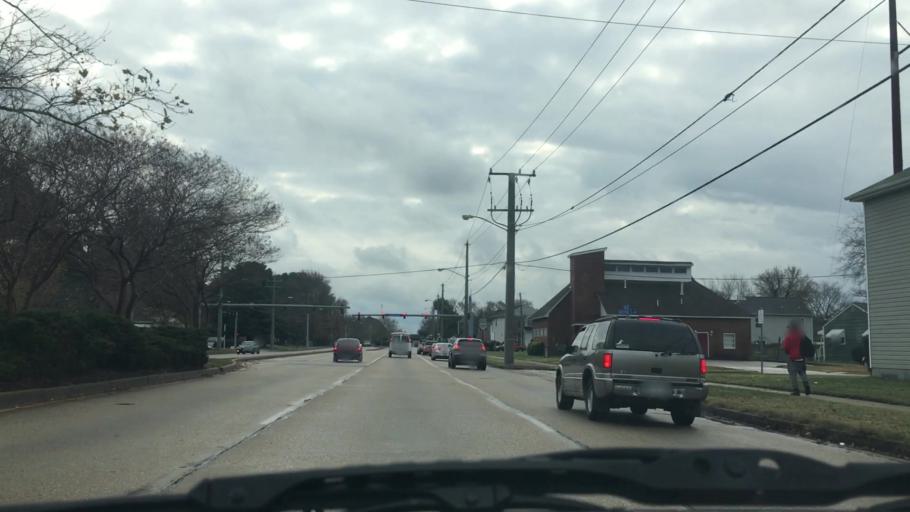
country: US
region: Virginia
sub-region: City of Norfolk
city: Norfolk
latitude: 36.9089
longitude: -76.2406
